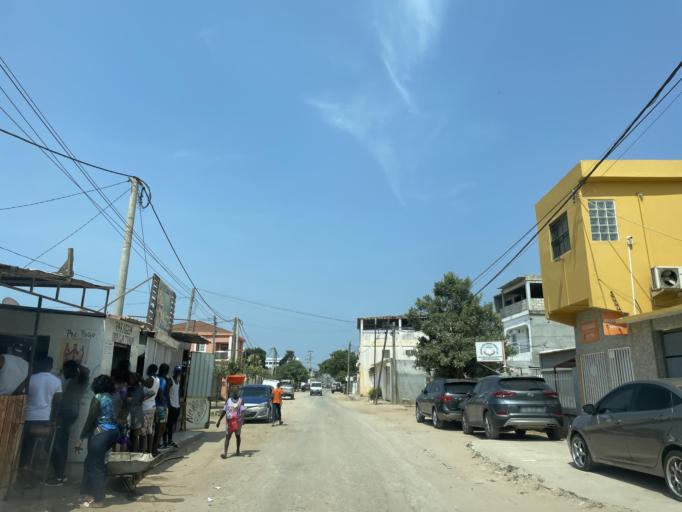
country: AO
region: Luanda
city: Luanda
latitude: -8.9003
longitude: 13.1834
